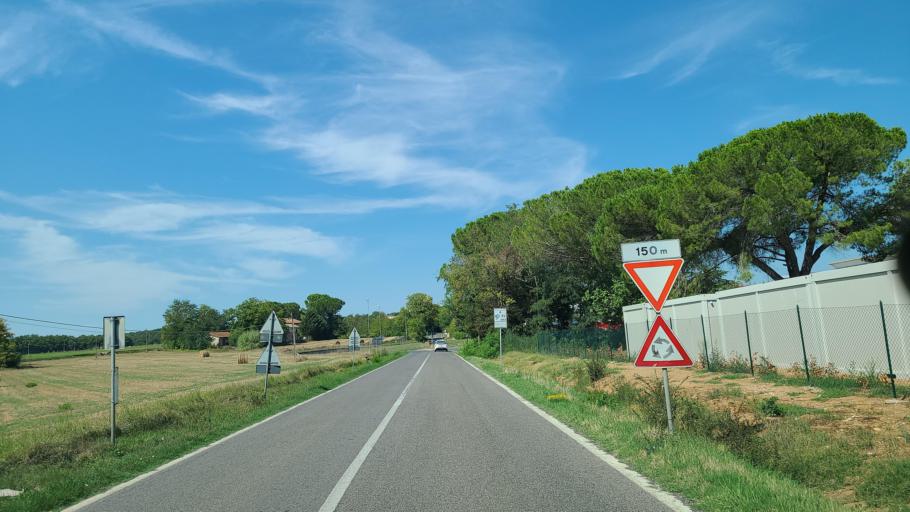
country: IT
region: Tuscany
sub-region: Provincia di Siena
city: Castellina Scalo
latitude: 43.3932
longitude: 11.1931
